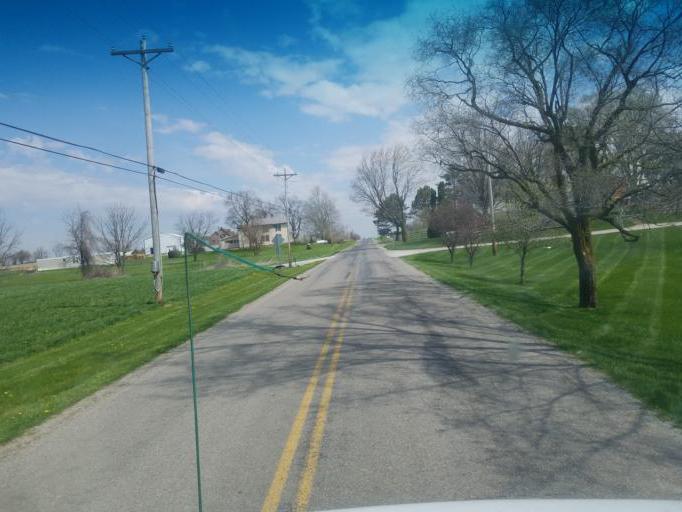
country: US
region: Ohio
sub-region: Hardin County
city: Kenton
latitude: 40.5916
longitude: -83.6742
